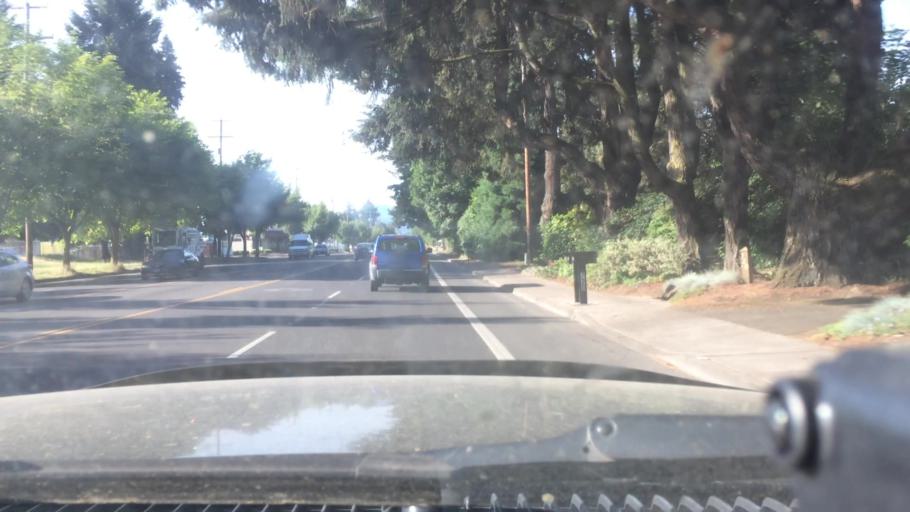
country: US
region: Oregon
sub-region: Lane County
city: Eugene
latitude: 44.0734
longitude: -123.1191
